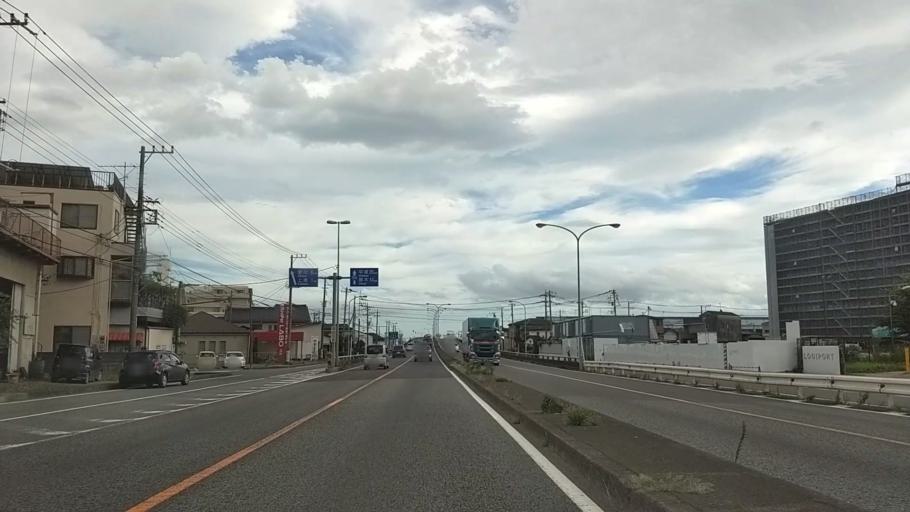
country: JP
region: Kanagawa
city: Zama
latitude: 35.5588
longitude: 139.3473
